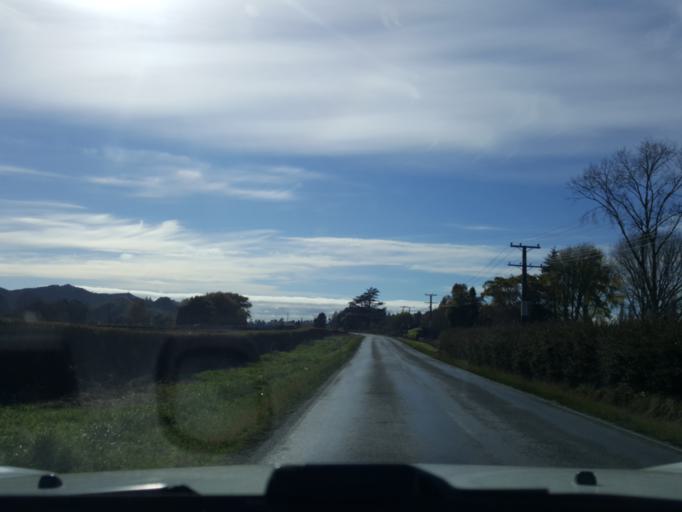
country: NZ
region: Waikato
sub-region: Waikato District
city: Ngaruawahia
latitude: -37.6032
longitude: 175.2003
